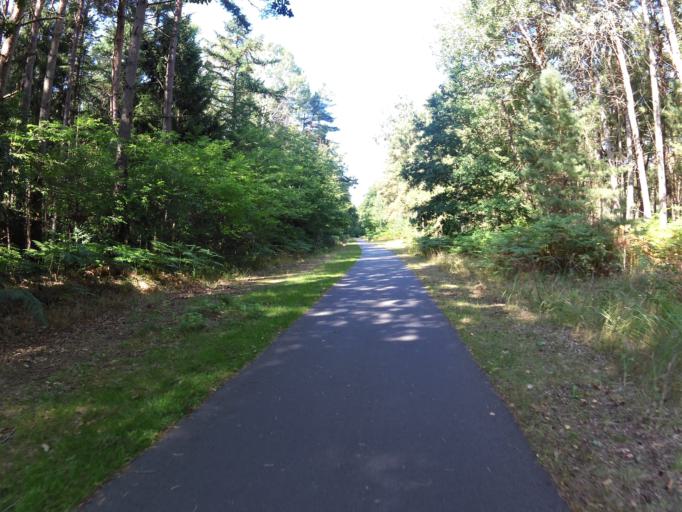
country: DE
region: Mecklenburg-Vorpommern
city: Karlshagen
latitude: 54.1369
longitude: 13.8157
